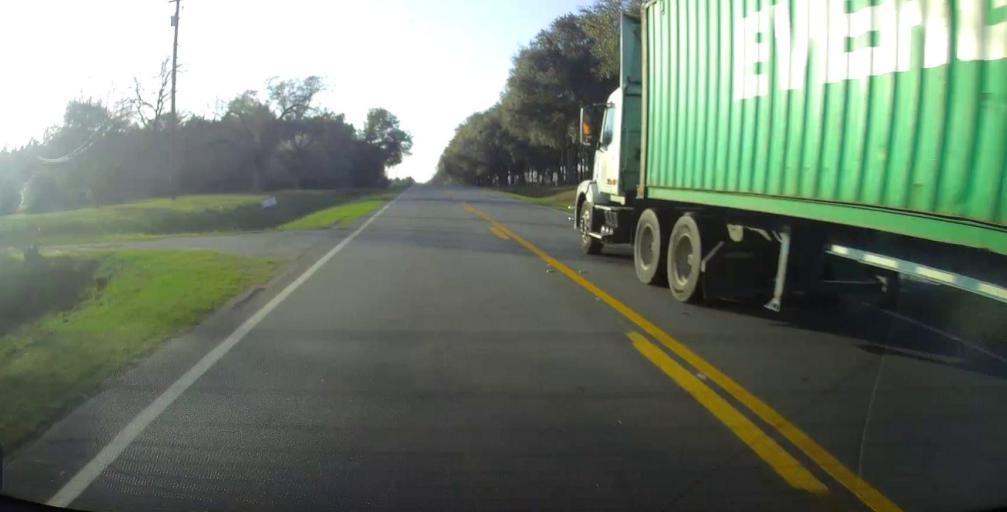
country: US
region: Georgia
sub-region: Evans County
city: Claxton
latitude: 32.1542
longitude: -81.8516
